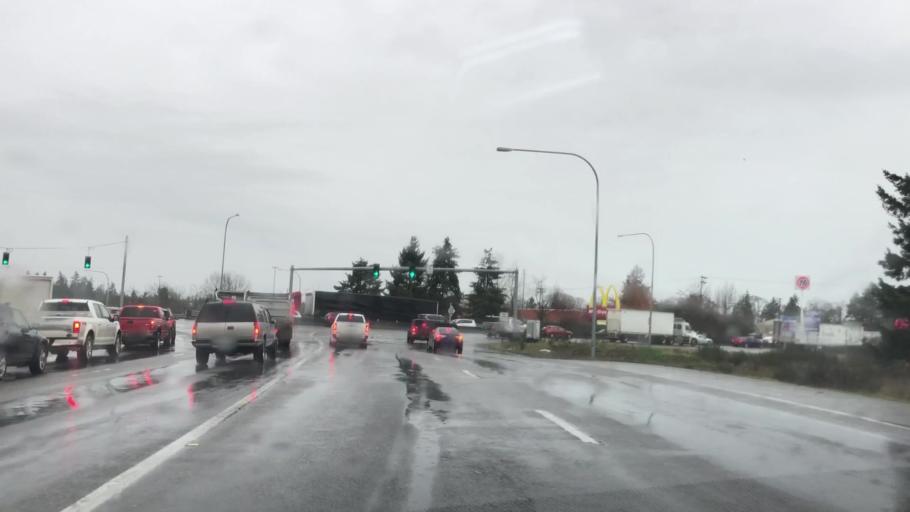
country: US
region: Washington
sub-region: Pierce County
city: McChord Air Force Base
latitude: 47.1643
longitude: -122.4811
